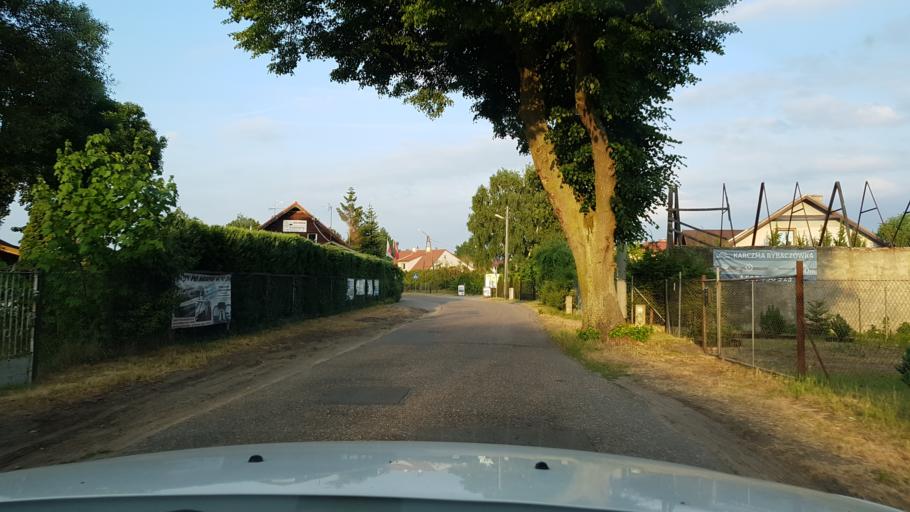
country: PL
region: West Pomeranian Voivodeship
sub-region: Swinoujscie
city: Swinoujscie
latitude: 53.8514
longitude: 14.2900
